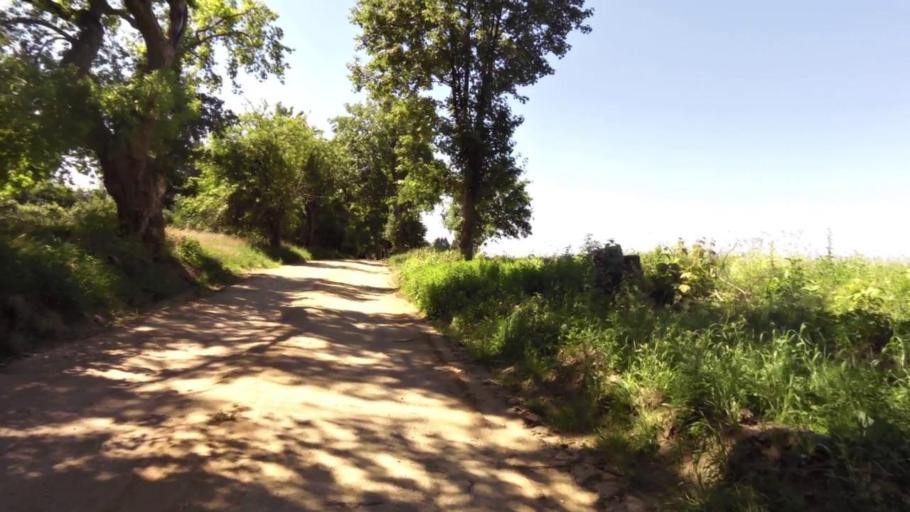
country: PL
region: West Pomeranian Voivodeship
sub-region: Powiat swidwinski
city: Rabino
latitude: 53.8775
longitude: 16.0070
